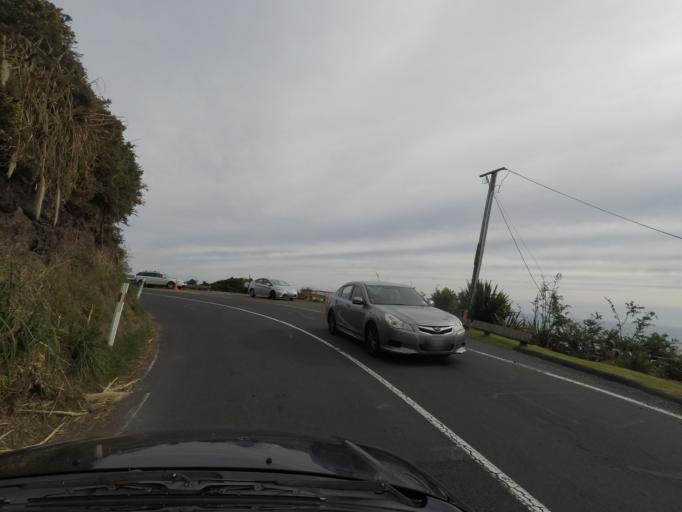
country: NZ
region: Auckland
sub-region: Auckland
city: Muriwai Beach
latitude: -36.9623
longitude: 174.4741
